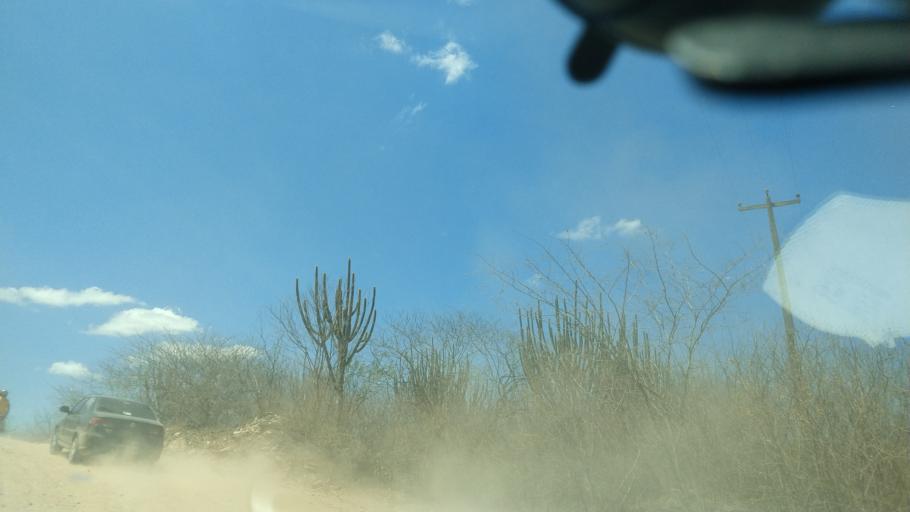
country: BR
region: Rio Grande do Norte
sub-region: Cerro Cora
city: Cerro Cora
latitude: -6.0099
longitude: -36.2806
